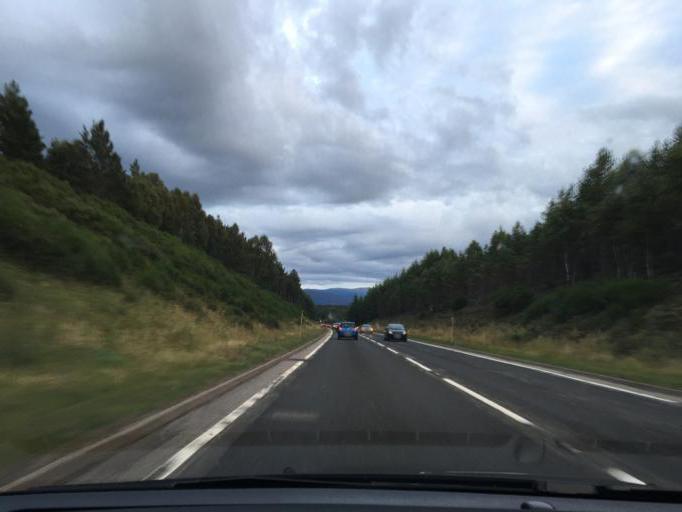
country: GB
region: Scotland
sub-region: Highland
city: Aviemore
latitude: 57.2876
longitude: -3.8439
